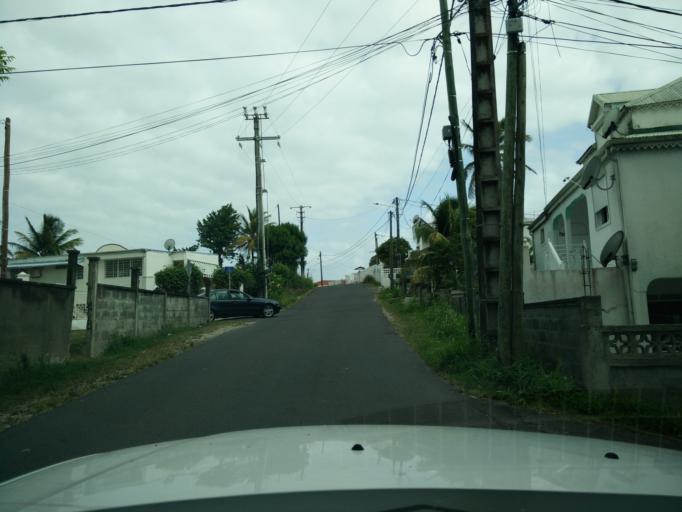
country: GP
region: Guadeloupe
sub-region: Guadeloupe
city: Sainte-Anne
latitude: 16.2215
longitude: -61.4335
